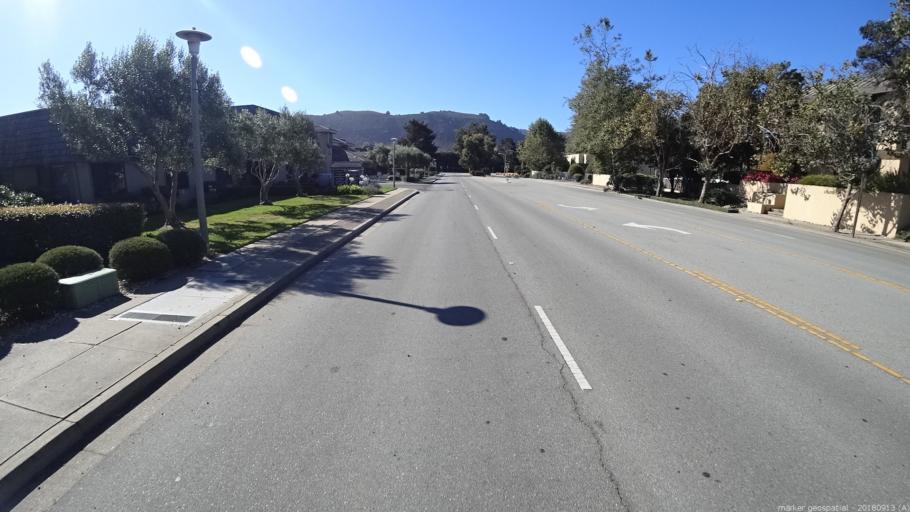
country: US
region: California
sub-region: Monterey County
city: Carmel-by-the-Sea
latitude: 36.5395
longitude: -121.9047
